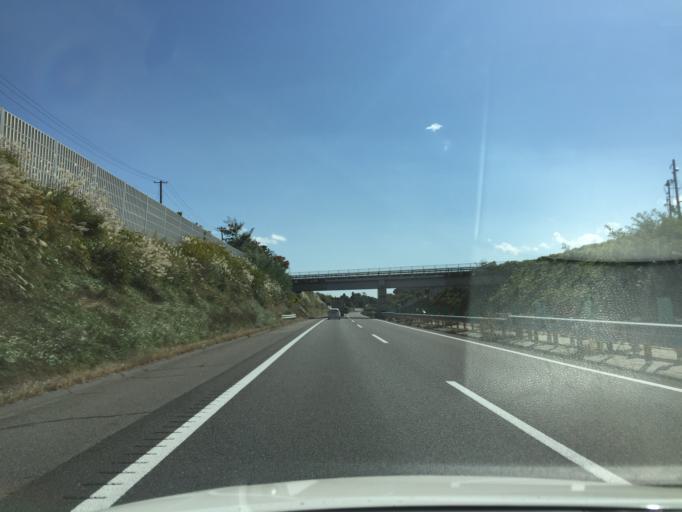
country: JP
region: Fukushima
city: Koriyama
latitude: 37.3449
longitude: 140.3319
